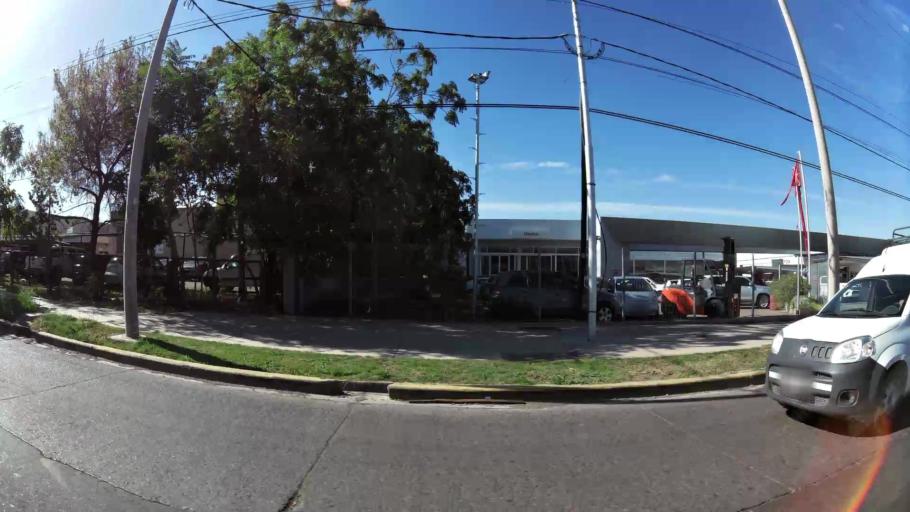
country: AR
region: Mendoza
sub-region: Departamento de Godoy Cruz
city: Godoy Cruz
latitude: -32.9275
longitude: -68.8187
